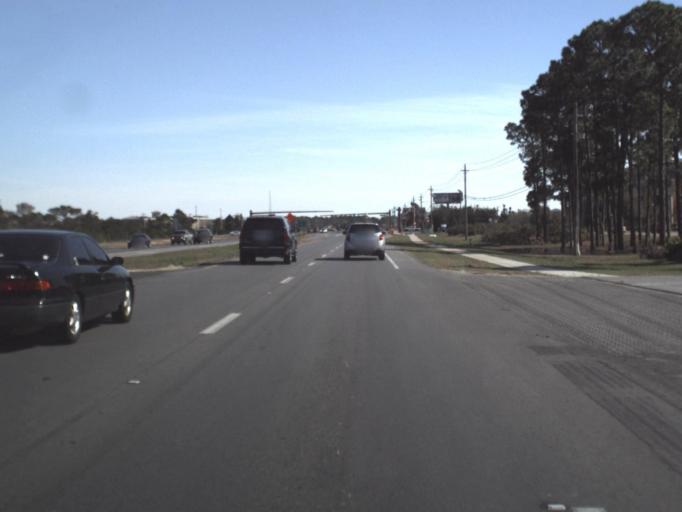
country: US
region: Florida
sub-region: Bay County
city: Panama City Beach
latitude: 30.2121
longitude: -85.8518
